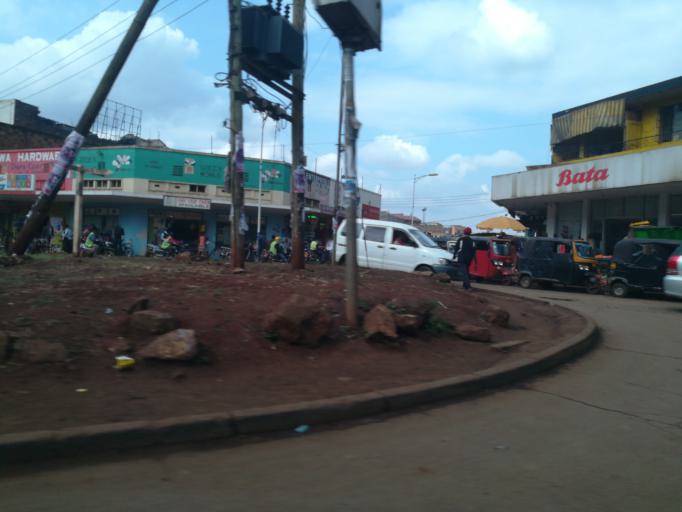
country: KE
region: Nairobi Area
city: Thika
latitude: -1.0355
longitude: 37.0755
